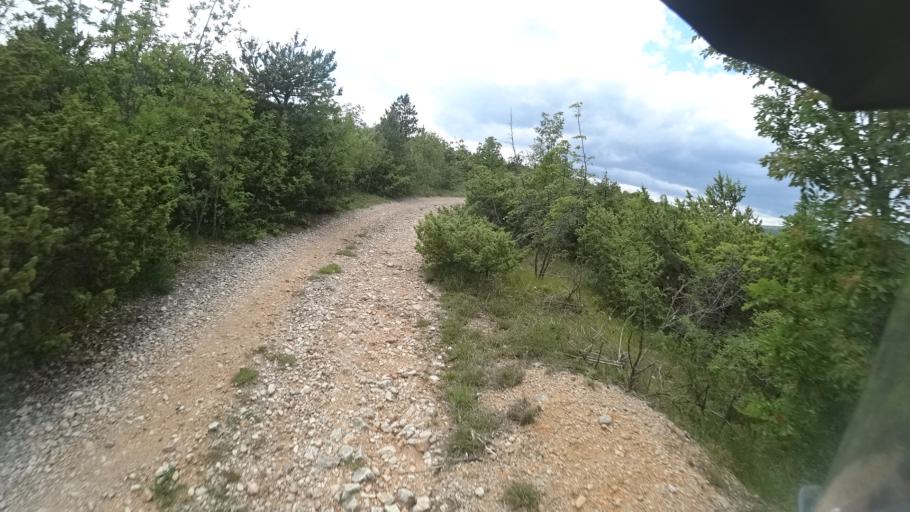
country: HR
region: Sibensko-Kniniska
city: Knin
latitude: 44.0932
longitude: 16.0789
